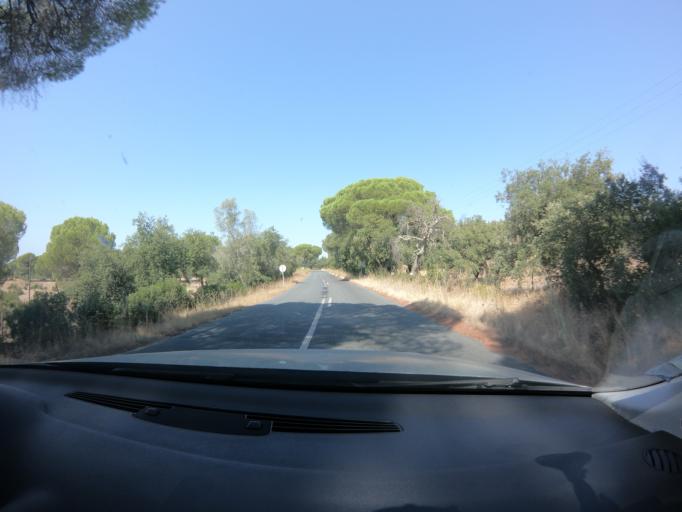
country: PT
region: Setubal
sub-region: Alcacer do Sal
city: Alcacer do Sal
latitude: 38.3011
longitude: -8.4050
